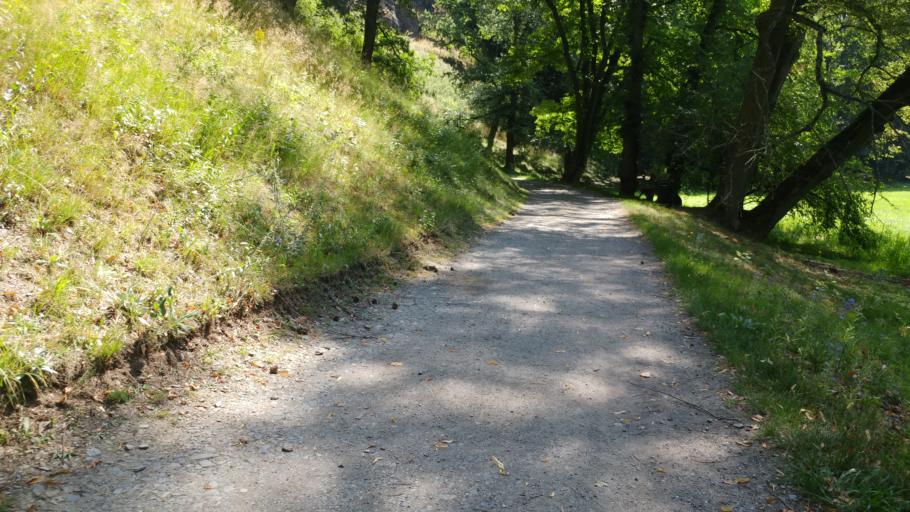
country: CZ
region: Central Bohemia
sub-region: Okres Praha-Zapad
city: Pruhonice
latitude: 49.9926
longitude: 14.5603
